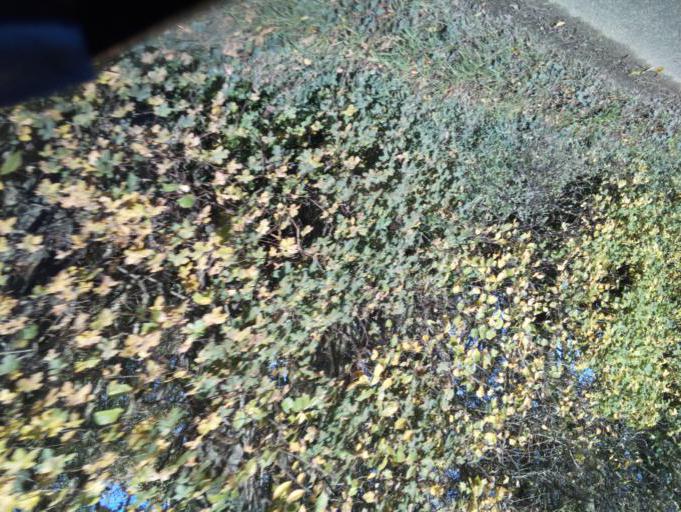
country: GB
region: England
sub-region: Somerset
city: Martock
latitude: 50.9840
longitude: -2.7548
